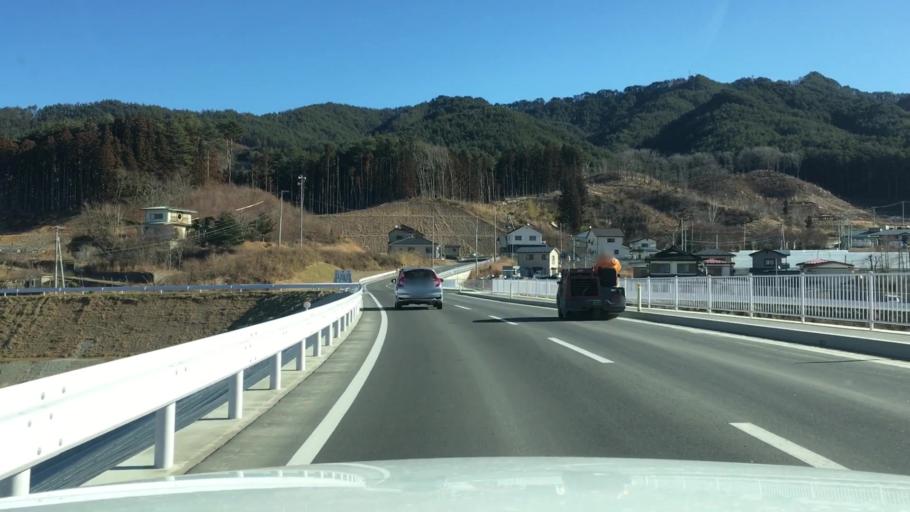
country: JP
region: Iwate
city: Yamada
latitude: 39.4373
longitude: 141.9795
